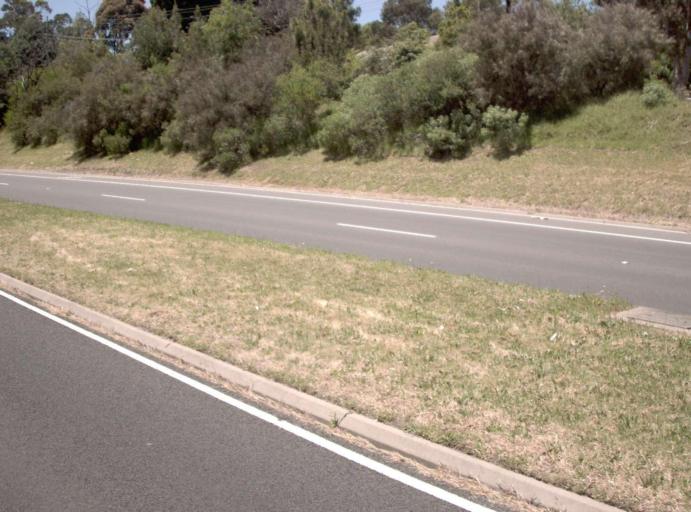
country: AU
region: Victoria
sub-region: Mornington Peninsula
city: Mount Eliza
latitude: -38.1688
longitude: 145.1014
